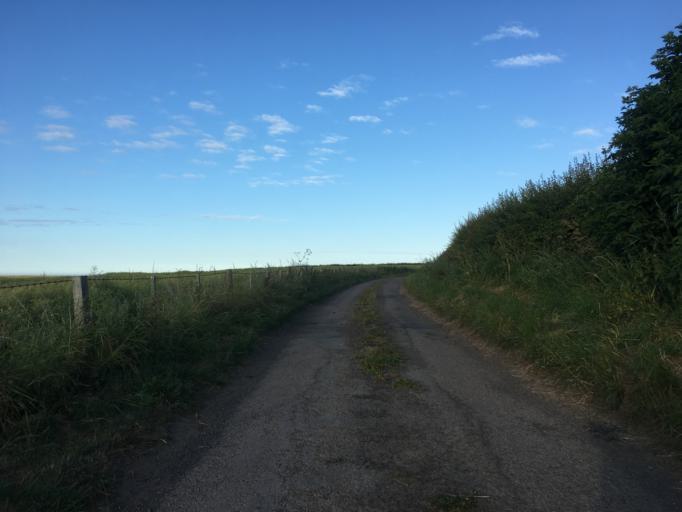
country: GB
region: England
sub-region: Northumberland
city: Bamburgh
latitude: 55.5922
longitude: -1.6955
